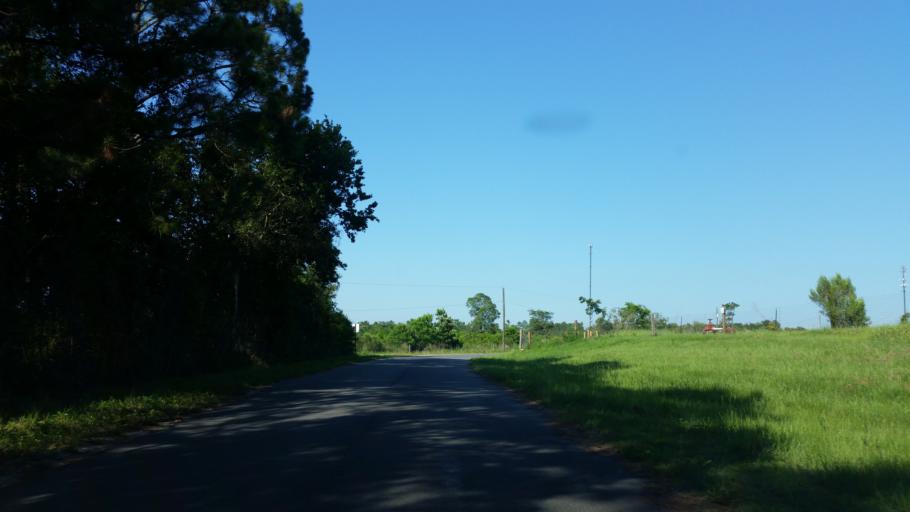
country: US
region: Florida
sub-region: Escambia County
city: Cantonment
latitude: 30.5795
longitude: -87.4028
